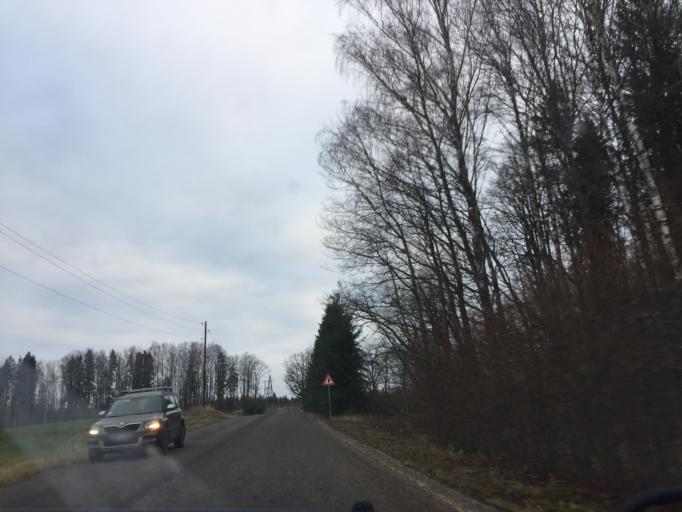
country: LV
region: Krimulda
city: Ragana
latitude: 57.1588
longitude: 24.7378
